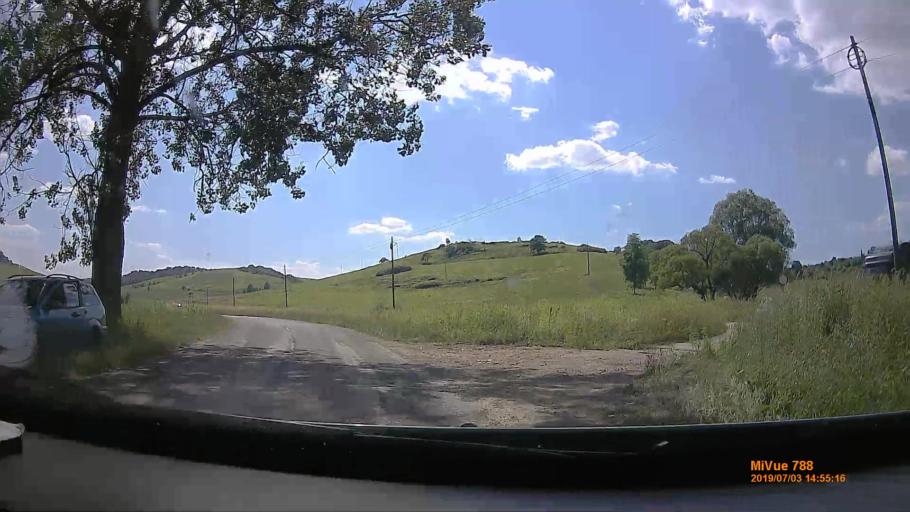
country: HU
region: Borsod-Abauj-Zemplen
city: Putnok
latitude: 48.2647
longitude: 20.4054
